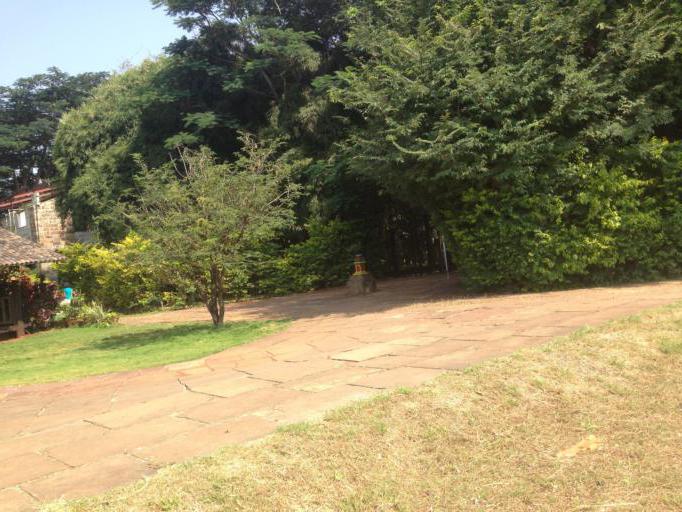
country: IN
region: Karnataka
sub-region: Belgaum
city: Belgaum
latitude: 15.8224
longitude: 74.4812
